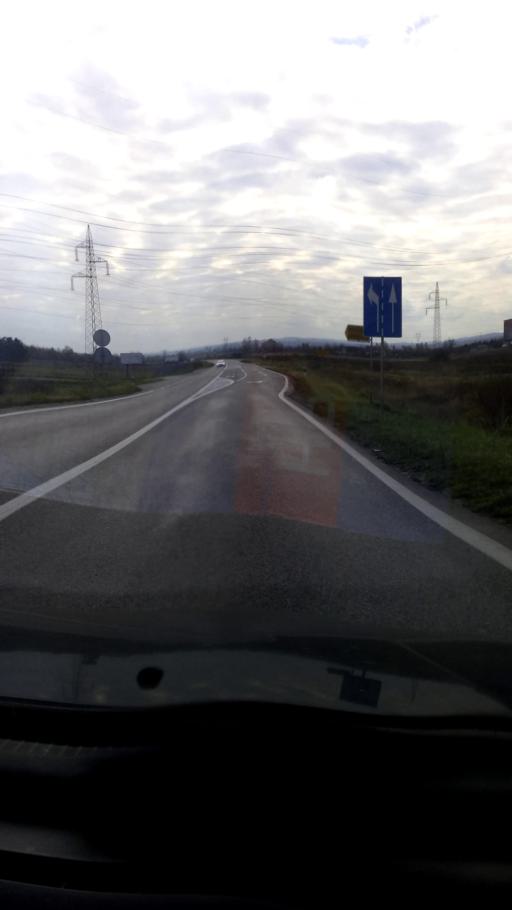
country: HR
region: Zagrebacka
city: Mraclin
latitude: 45.6741
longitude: 16.1179
